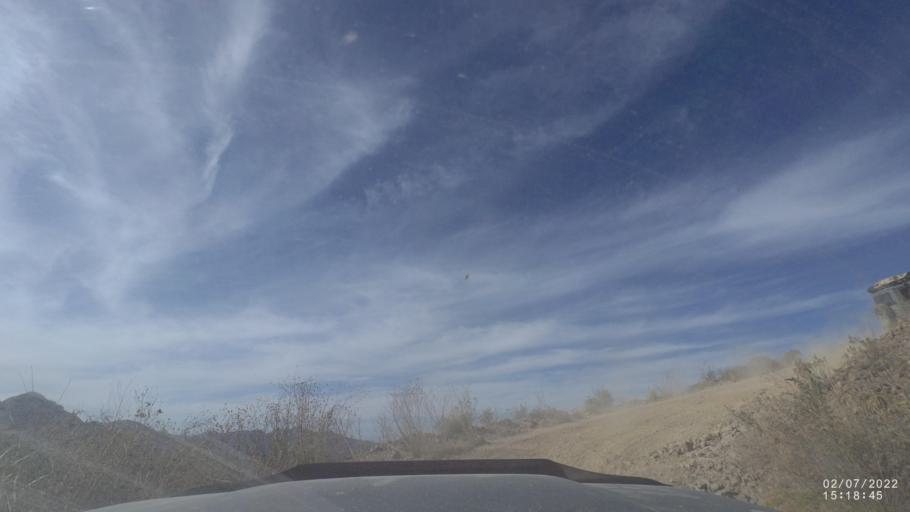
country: BO
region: Cochabamba
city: Irpa Irpa
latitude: -17.8651
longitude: -66.4298
